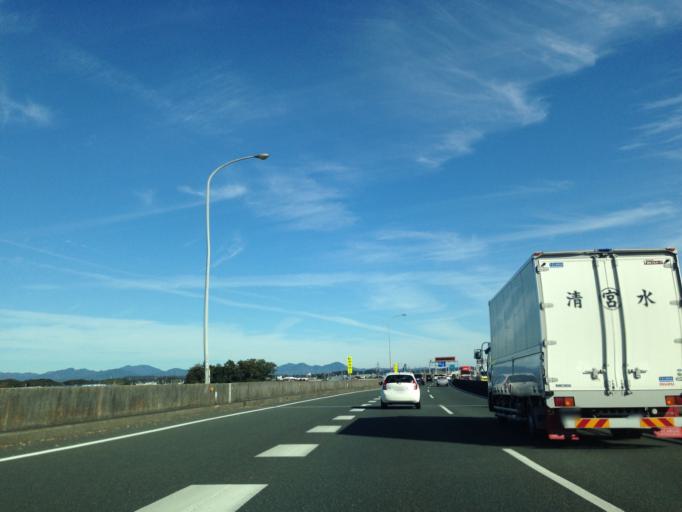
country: JP
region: Shizuoka
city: Fukuroi
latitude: 34.7490
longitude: 137.8971
